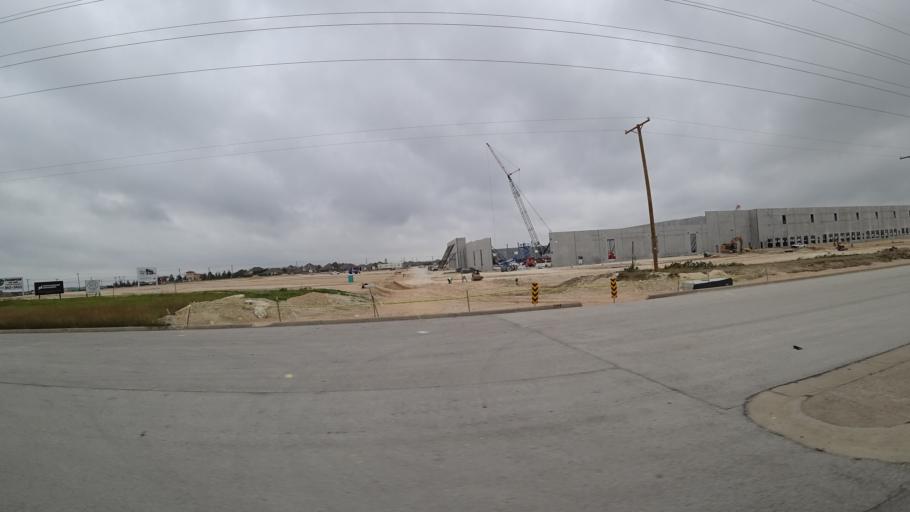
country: US
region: Texas
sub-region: Travis County
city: Windemere
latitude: 30.4843
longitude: -97.6170
